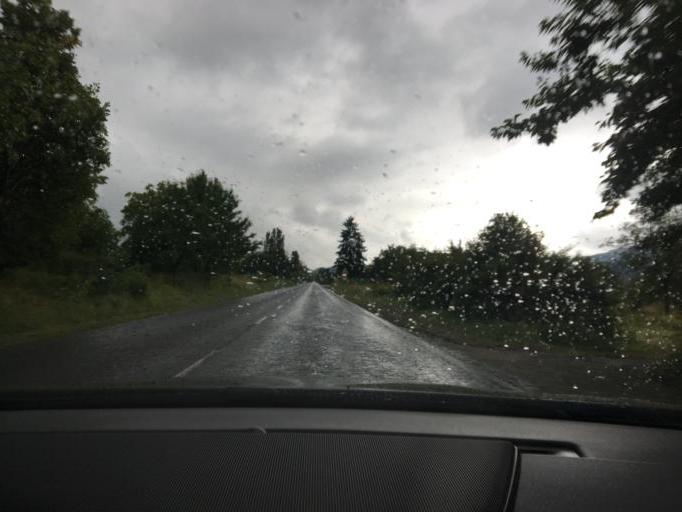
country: BG
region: Kyustendil
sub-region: Obshtina Kyustendil
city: Kyustendil
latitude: 42.2664
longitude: 22.6091
